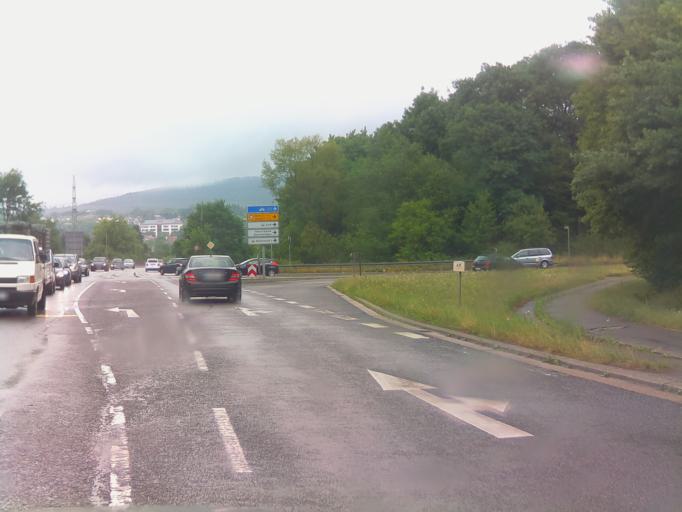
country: DE
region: Saarland
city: Saarwellingen
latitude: 49.3686
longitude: 6.7944
